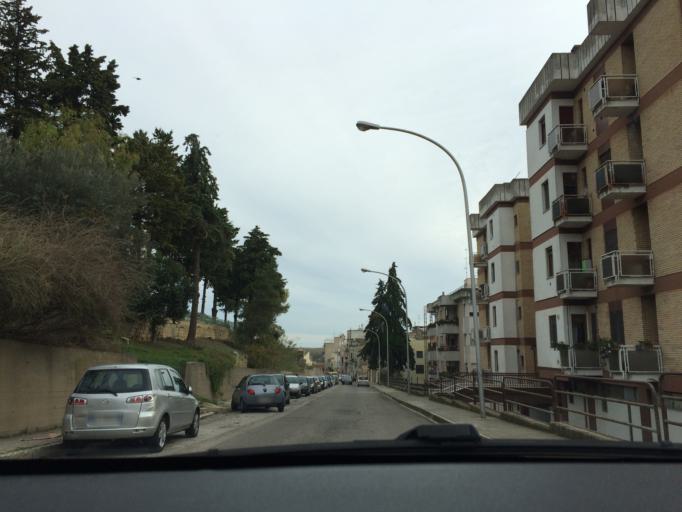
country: IT
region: Basilicate
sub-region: Provincia di Matera
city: Matera
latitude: 40.6621
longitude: 16.6048
